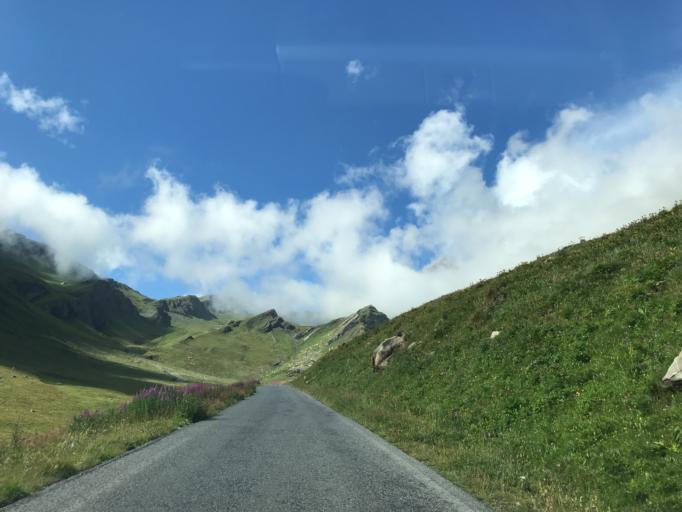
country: IT
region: Piedmont
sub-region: Provincia di Cuneo
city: Pontechianale
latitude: 44.6638
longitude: 6.9869
